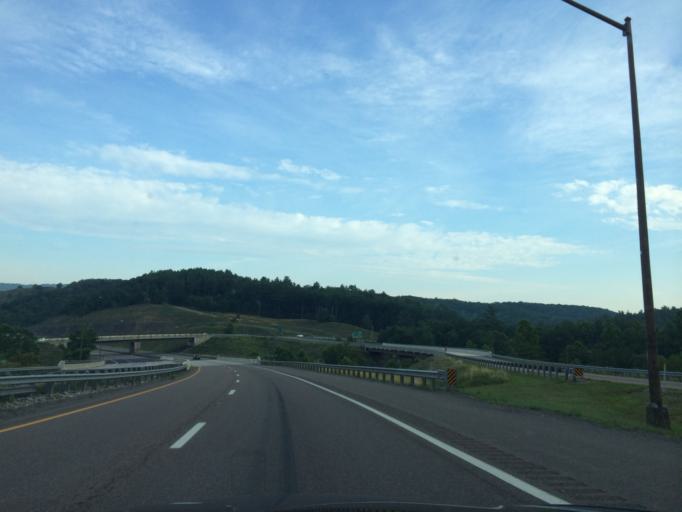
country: US
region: West Virginia
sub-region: Morgan County
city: Berkeley Springs
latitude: 39.6743
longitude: -78.4565
